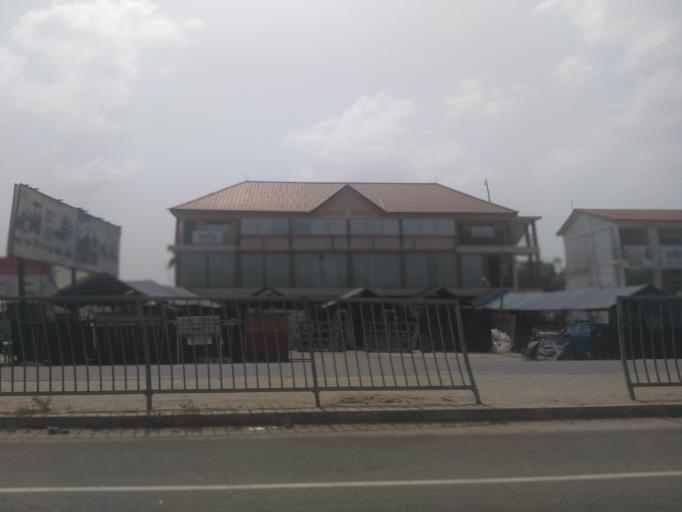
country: GH
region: Greater Accra
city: Dome
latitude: 5.6168
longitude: -0.2002
